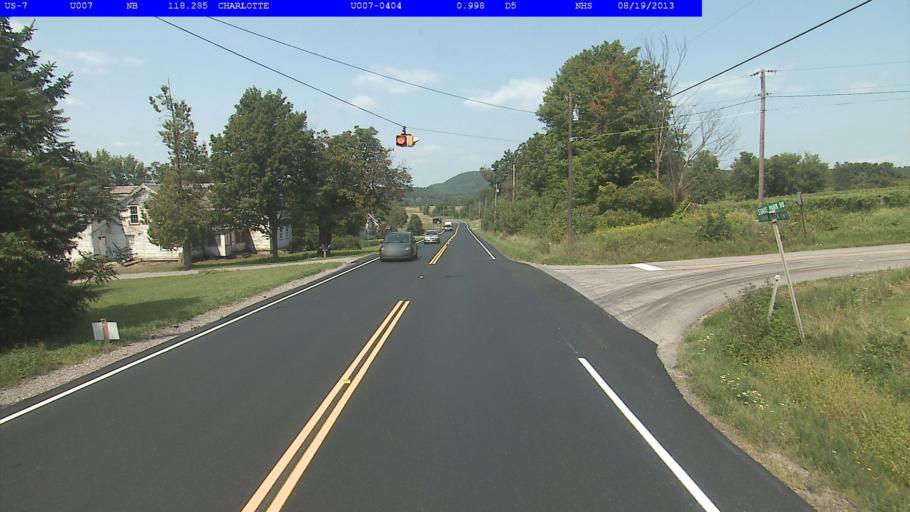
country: US
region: Vermont
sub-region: Addison County
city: Vergennes
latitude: 44.2765
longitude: -73.2348
